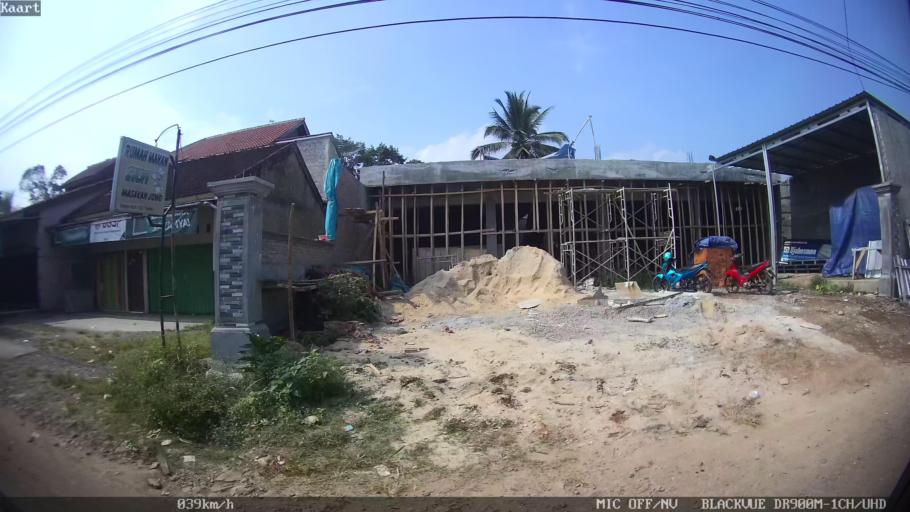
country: ID
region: Lampung
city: Gedongtataan
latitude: -5.3659
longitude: 105.1488
